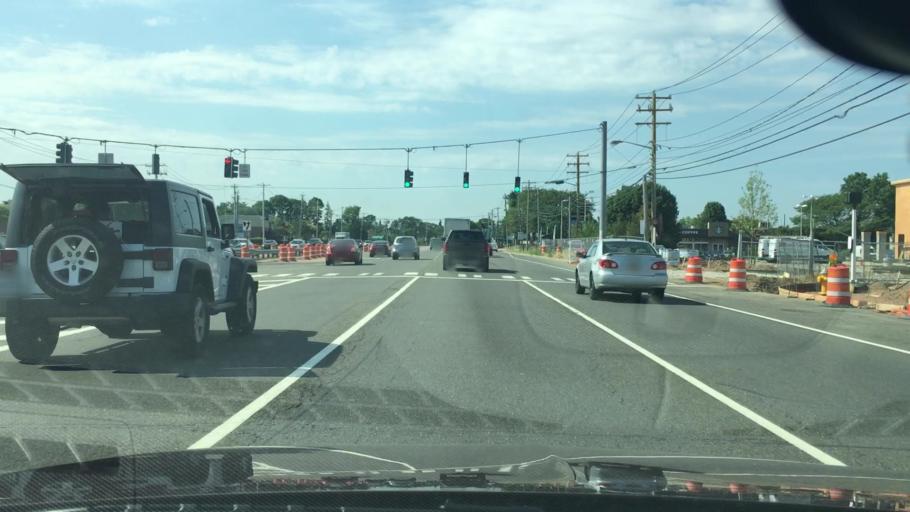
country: US
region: New York
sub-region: Suffolk County
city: East Farmingdale
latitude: 40.7286
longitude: -73.4240
